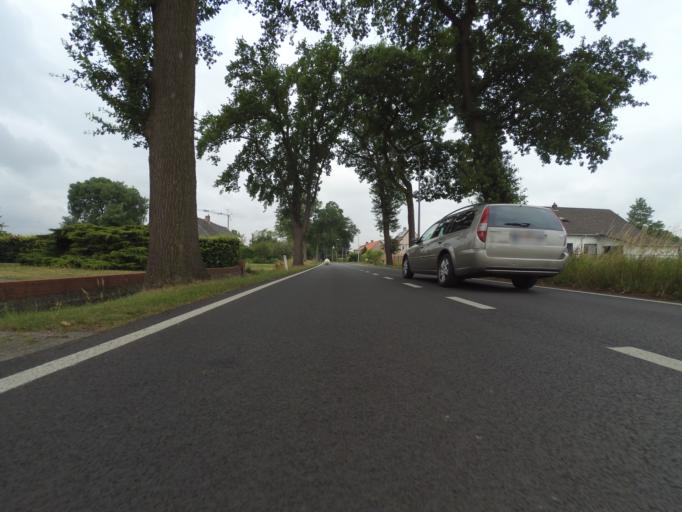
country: BE
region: Flanders
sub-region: Provincie Antwerpen
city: Essen
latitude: 51.4445
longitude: 4.4069
